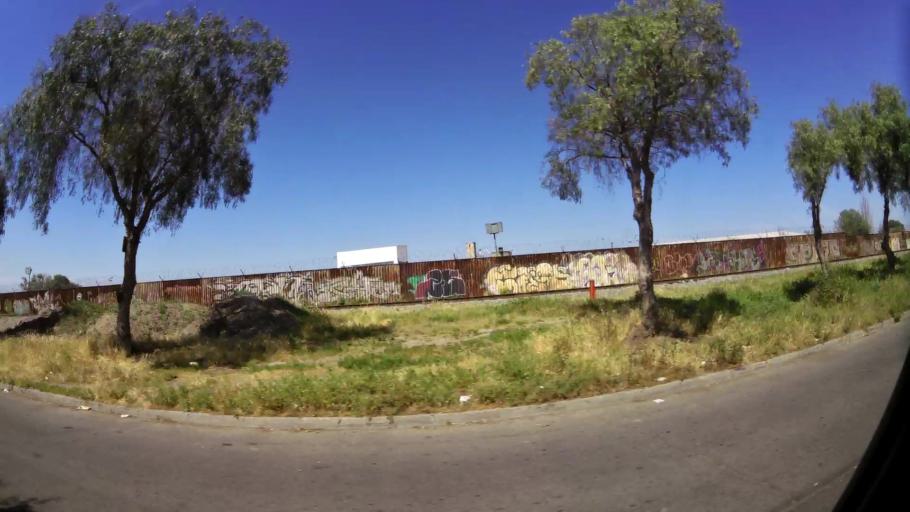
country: CL
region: Santiago Metropolitan
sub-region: Provincia de Santiago
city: Lo Prado
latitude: -33.5174
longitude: -70.7458
